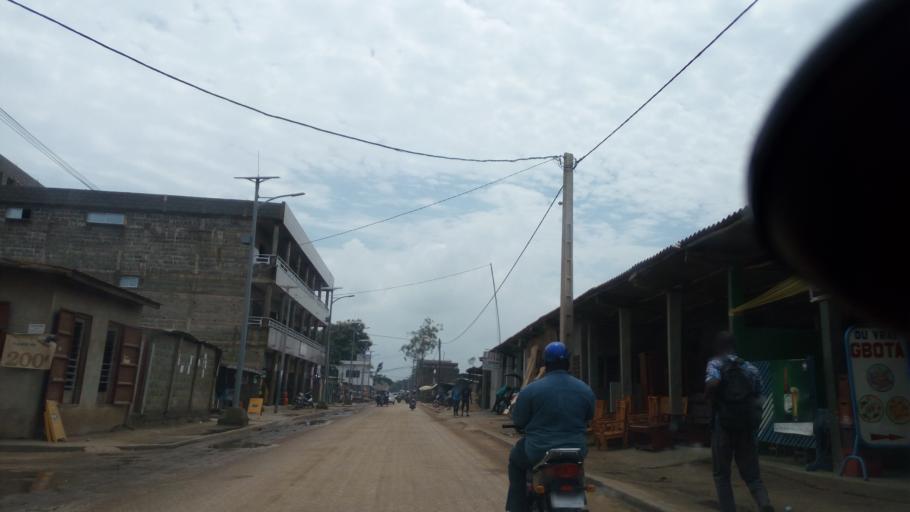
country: BJ
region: Atlantique
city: Abomey-Calavi
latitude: 6.3834
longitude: 2.3420
